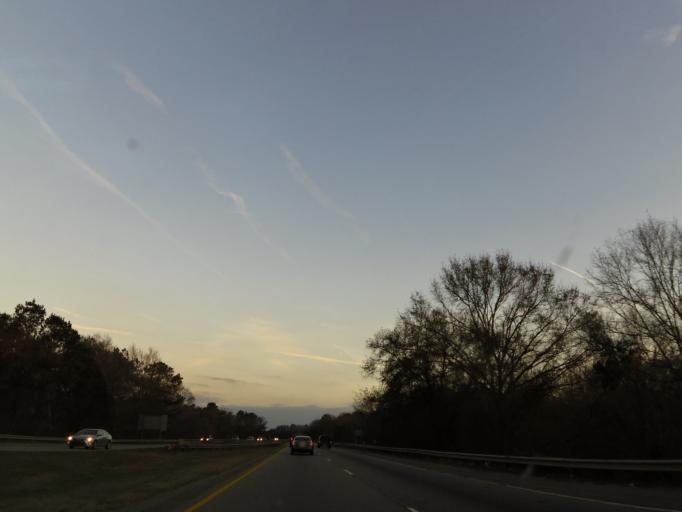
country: US
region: Georgia
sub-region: Dougherty County
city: Albany
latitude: 31.5992
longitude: -84.1439
